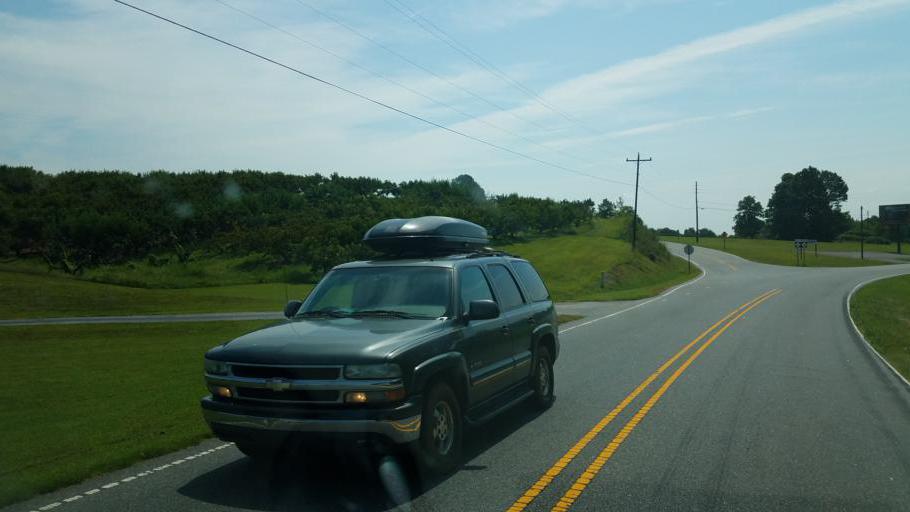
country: US
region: North Carolina
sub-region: Burke County
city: Icard
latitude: 35.5553
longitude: -81.5045
